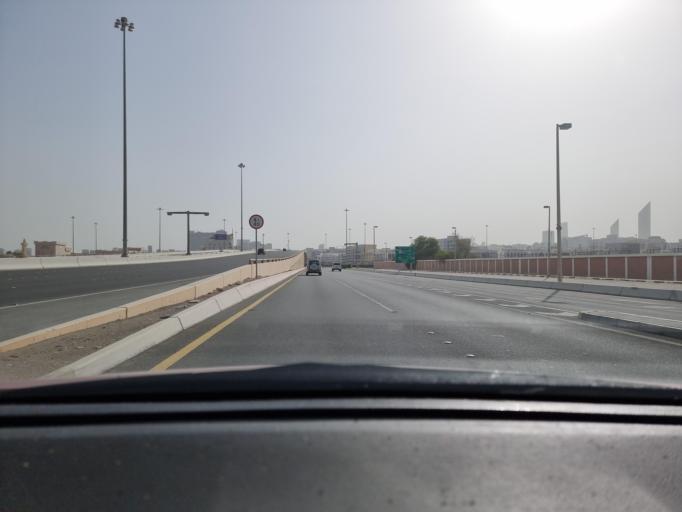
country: AE
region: Abu Dhabi
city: Abu Dhabi
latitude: 24.4820
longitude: 54.3897
